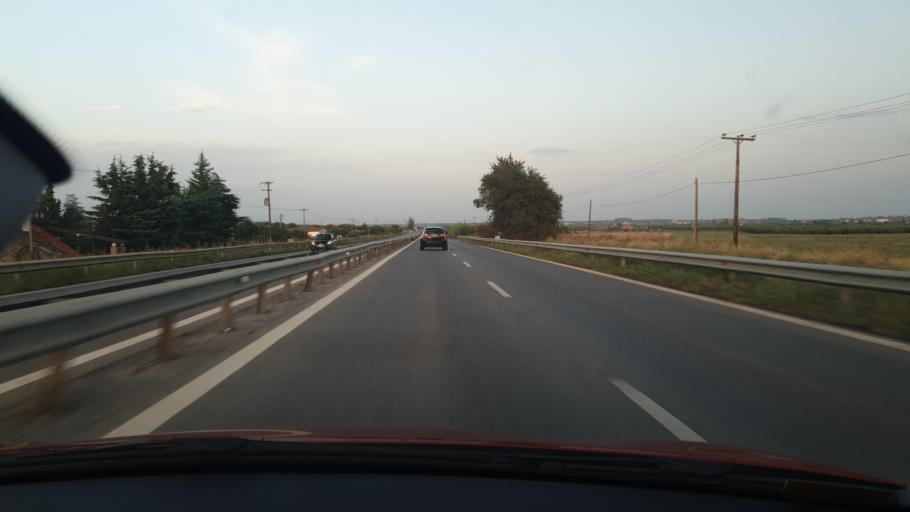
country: GR
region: Central Macedonia
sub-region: Nomos Chalkidikis
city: Nea Plagia
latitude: 40.2845
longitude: 23.1734
